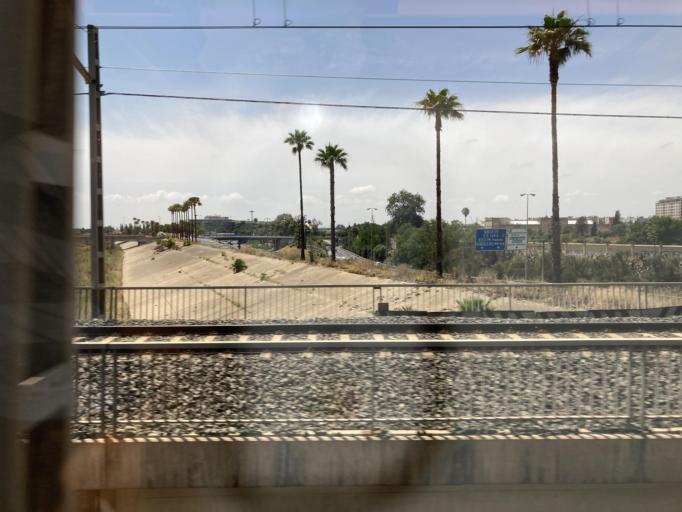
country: ES
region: Andalusia
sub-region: Provincia de Sevilla
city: Sevilla
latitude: 37.3431
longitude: -5.9675
